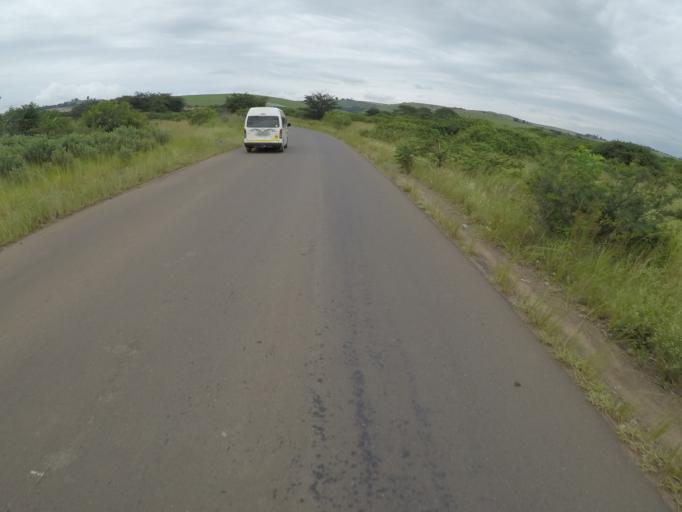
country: ZA
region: KwaZulu-Natal
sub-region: uThungulu District Municipality
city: Empangeni
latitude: -28.7212
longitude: 31.8676
